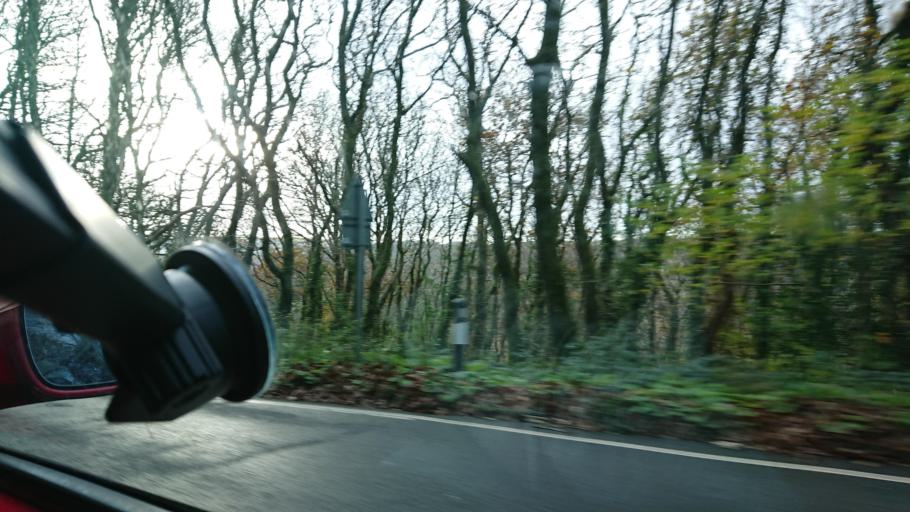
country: GB
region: England
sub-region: Cornwall
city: Looe
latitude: 50.3657
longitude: -4.4558
